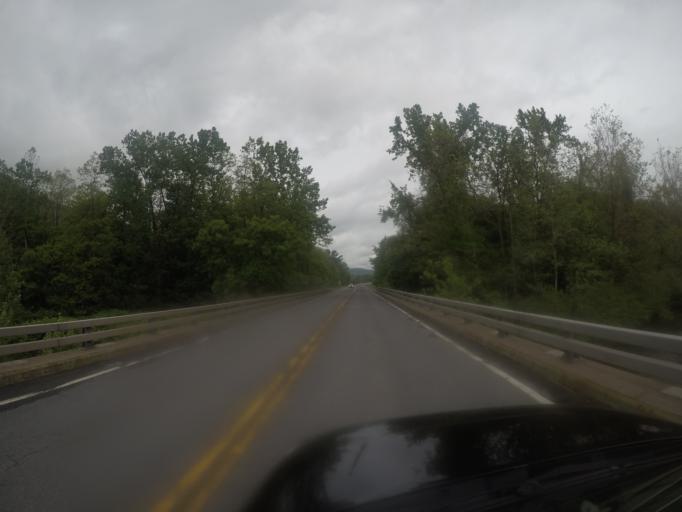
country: US
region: New York
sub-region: Ulster County
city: Shokan
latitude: 42.0413
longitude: -74.2808
